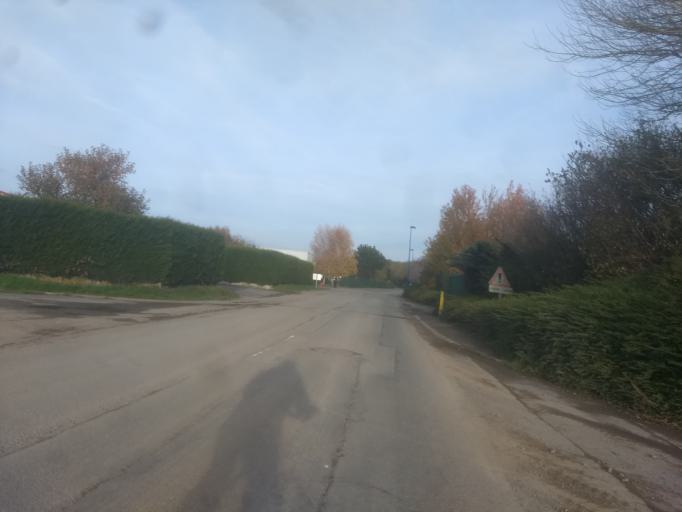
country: FR
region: Nord-Pas-de-Calais
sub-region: Departement du Pas-de-Calais
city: Beaurains
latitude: 50.2563
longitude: 2.7790
